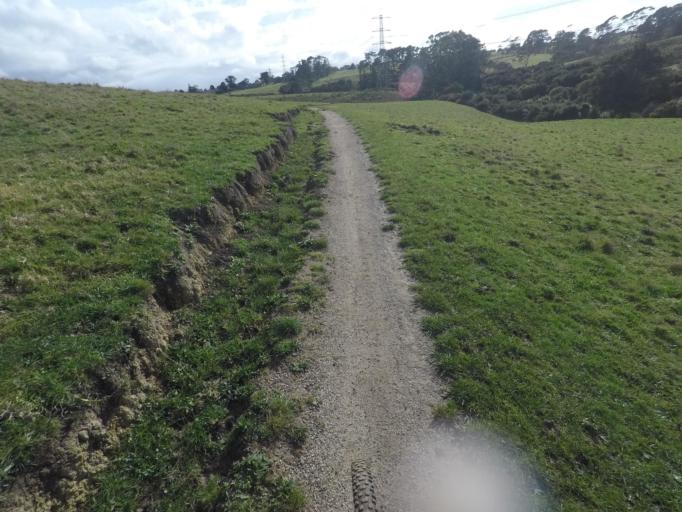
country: NZ
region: Auckland
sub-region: Auckland
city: Manukau City
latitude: -36.9969
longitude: 174.9099
